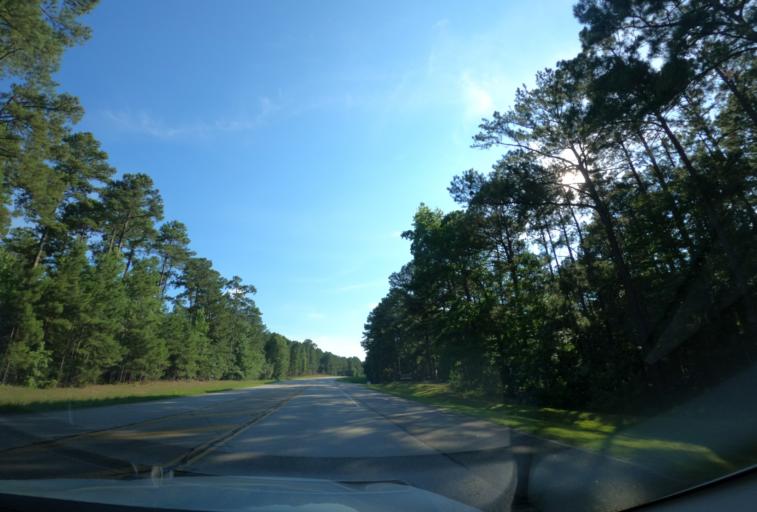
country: US
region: Georgia
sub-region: Lincoln County
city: Lincolnton
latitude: 33.8500
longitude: -82.3970
